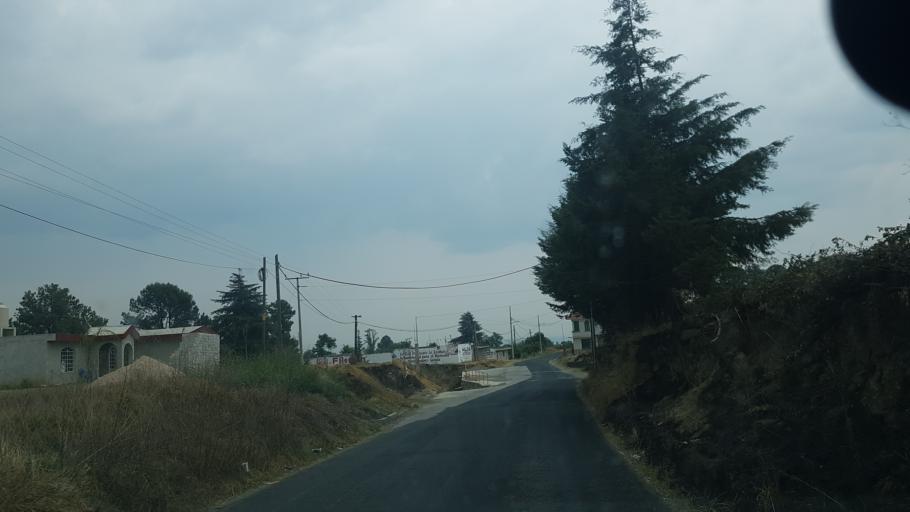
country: MX
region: Puebla
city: San Lorenzo Chiautzingo
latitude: 19.1948
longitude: -98.4662
